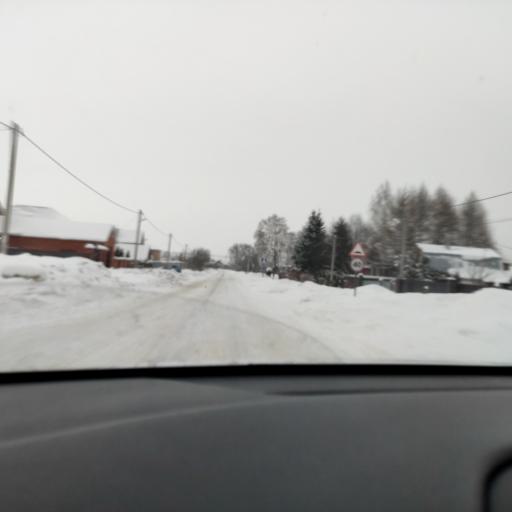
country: RU
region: Tatarstan
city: Vysokaya Gora
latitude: 55.9666
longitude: 49.1732
